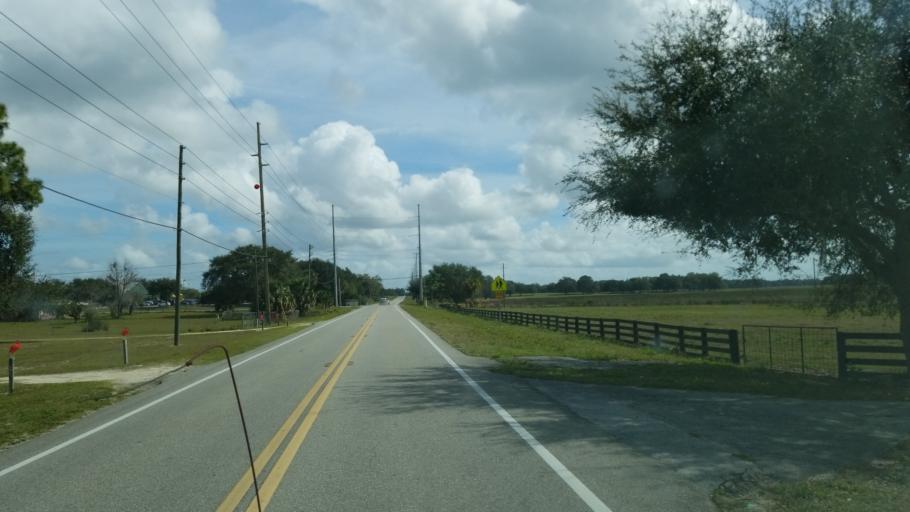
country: US
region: Florida
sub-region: Polk County
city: Dundee
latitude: 28.0410
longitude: -81.5642
